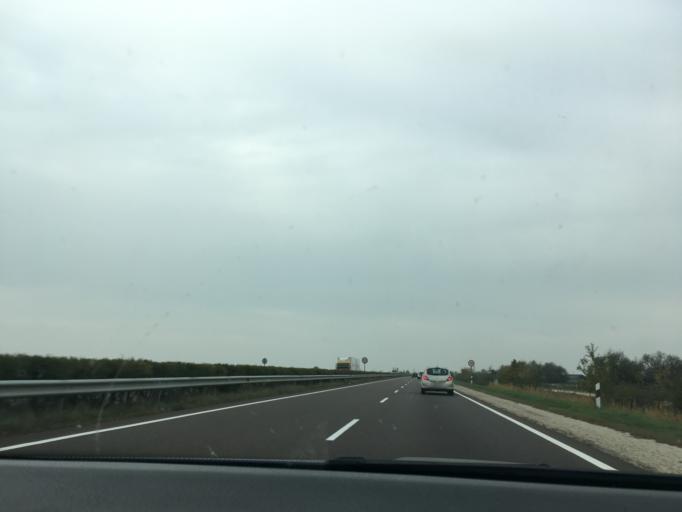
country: HU
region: Pest
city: Cegled
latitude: 47.1912
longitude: 19.8626
